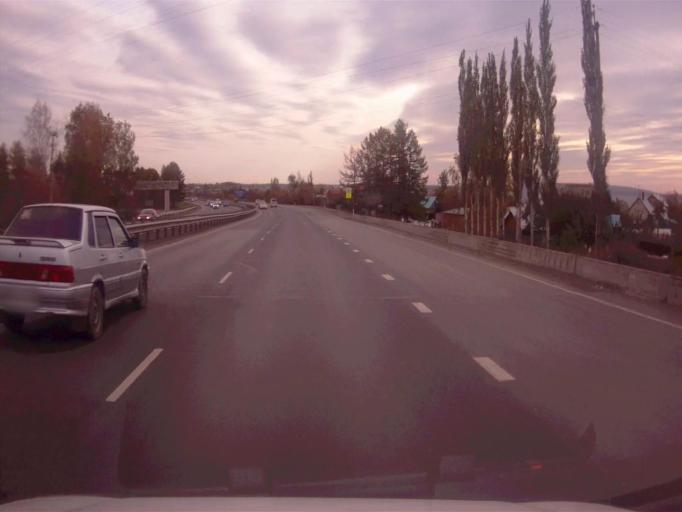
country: RU
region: Chelyabinsk
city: Novosineglazovskiy
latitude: 55.0368
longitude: 61.4416
